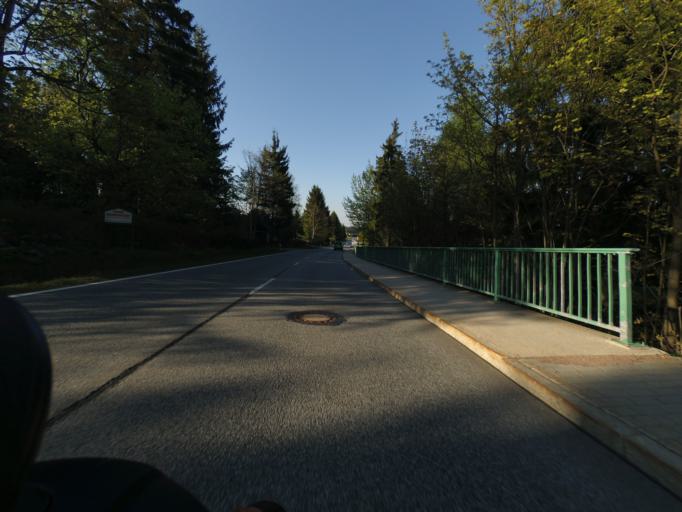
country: DE
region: Saxony
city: Altenberg
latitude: 50.7620
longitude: 13.7506
